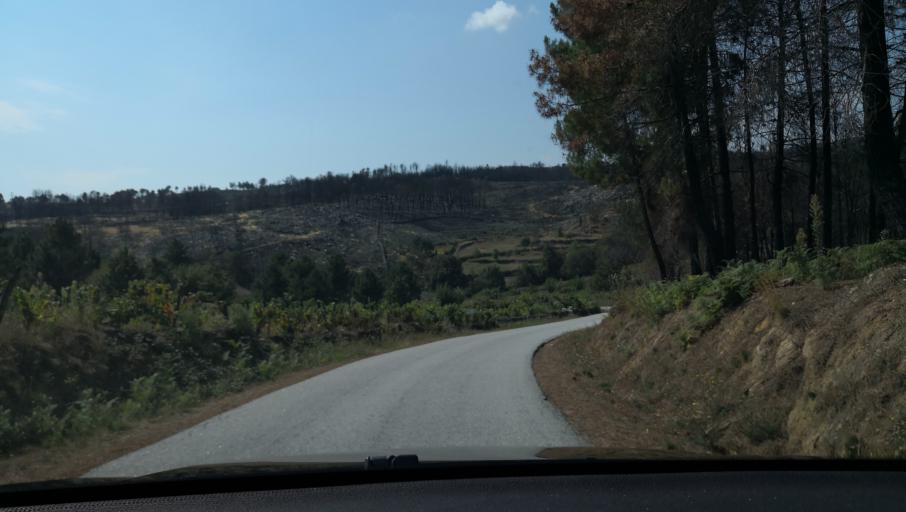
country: PT
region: Vila Real
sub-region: Sabrosa
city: Sabrosa
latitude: 41.3452
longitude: -7.5953
